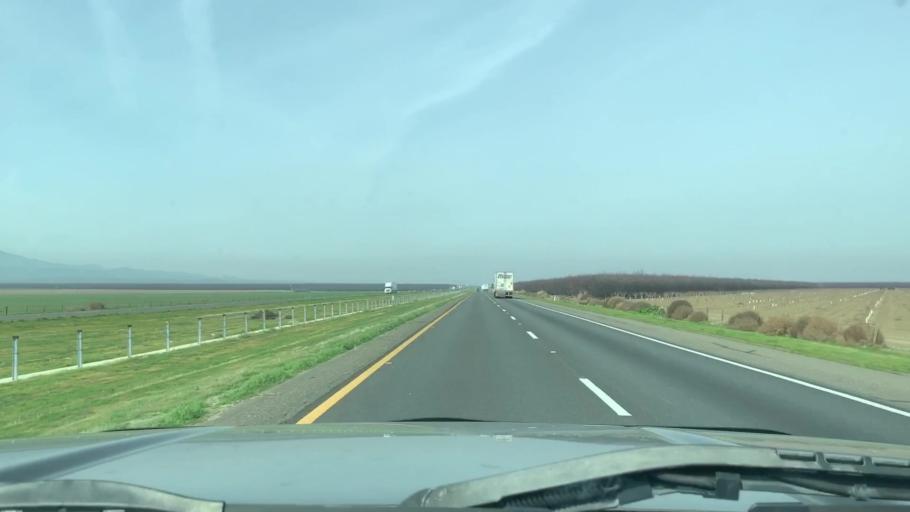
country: US
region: California
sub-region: Fresno County
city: Huron
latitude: 36.2179
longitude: -120.2209
